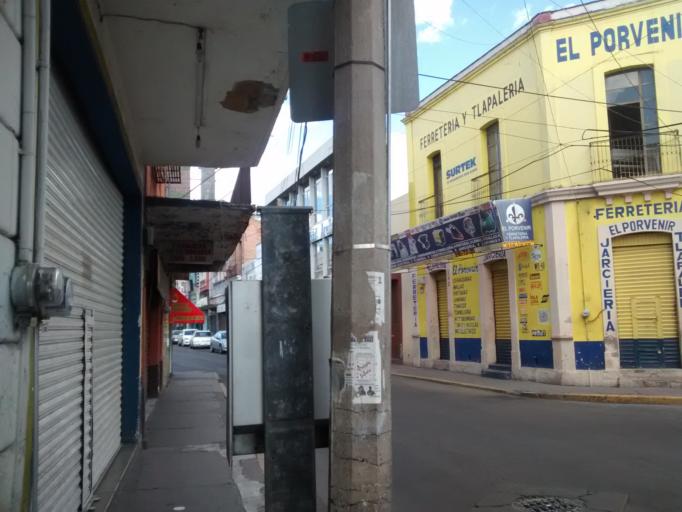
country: MX
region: Aguascalientes
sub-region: Aguascalientes
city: Aguascalientes
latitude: 21.8833
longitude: -102.2992
